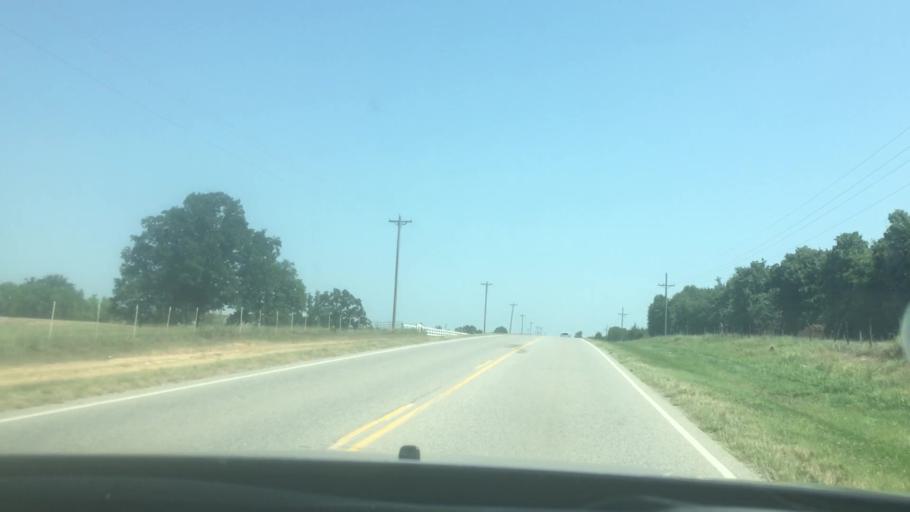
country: US
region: Oklahoma
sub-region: Johnston County
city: Tishomingo
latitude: 34.2450
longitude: -96.4248
